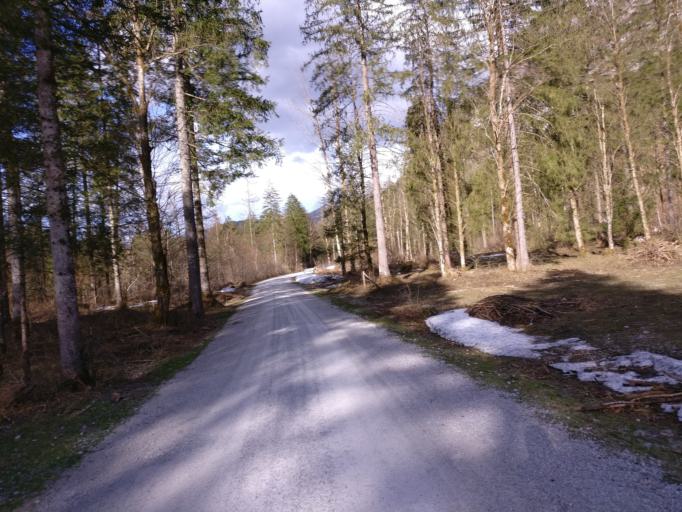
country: AT
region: Salzburg
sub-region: Politischer Bezirk Hallein
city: Golling an der Salzach
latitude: 47.5757
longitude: 13.1391
